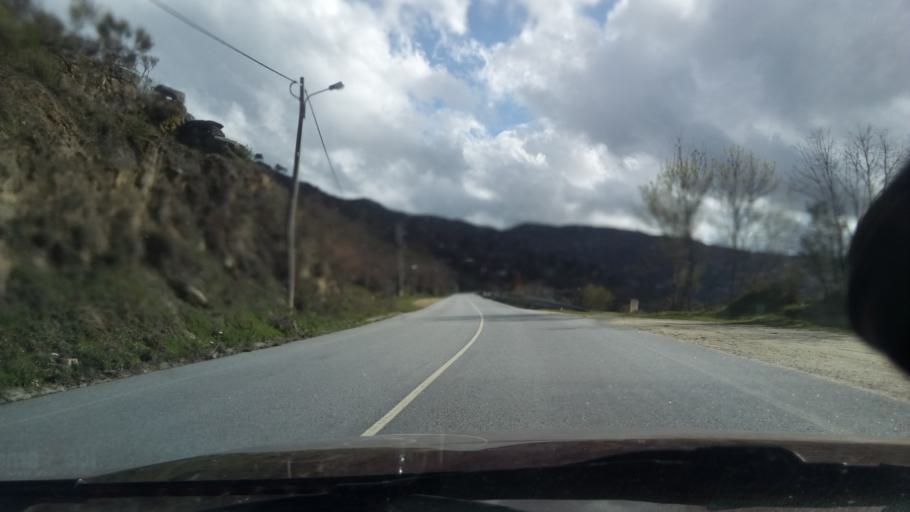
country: PT
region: Guarda
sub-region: Guarda
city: Guarda
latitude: 40.5742
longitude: -7.2973
